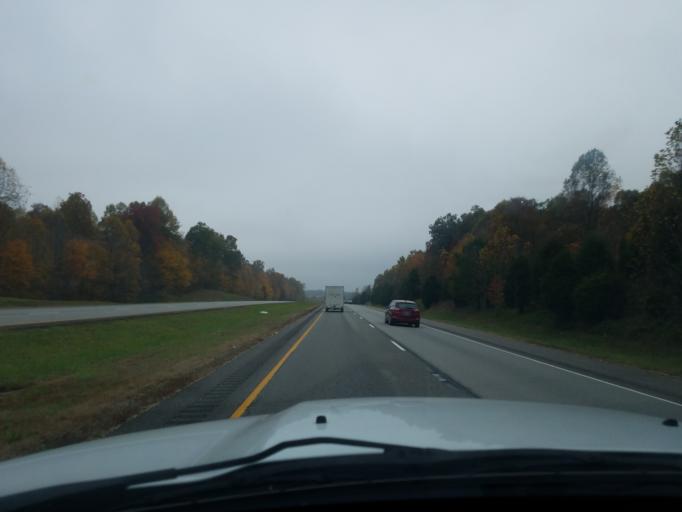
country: US
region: Kentucky
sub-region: Hardin County
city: Elizabethtown
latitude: 37.6351
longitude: -85.8294
